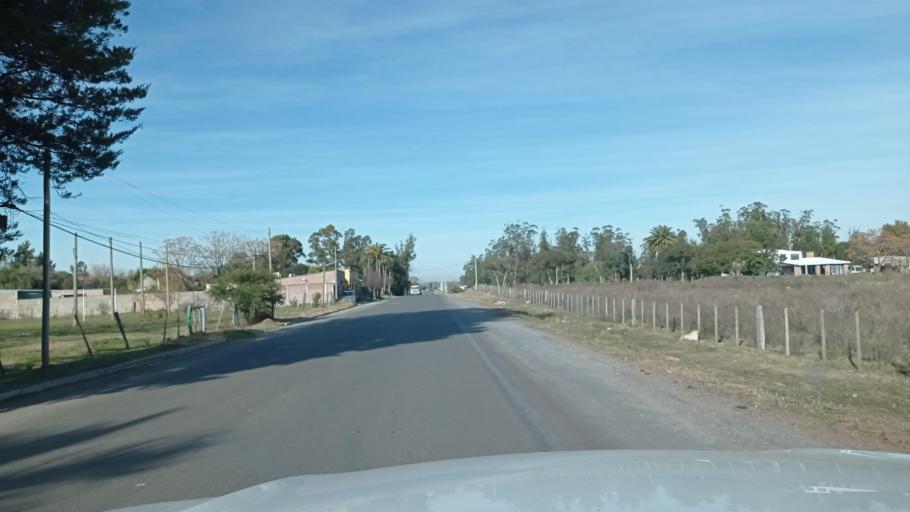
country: UY
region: Florida
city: Florida
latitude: -34.0928
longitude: -56.2394
